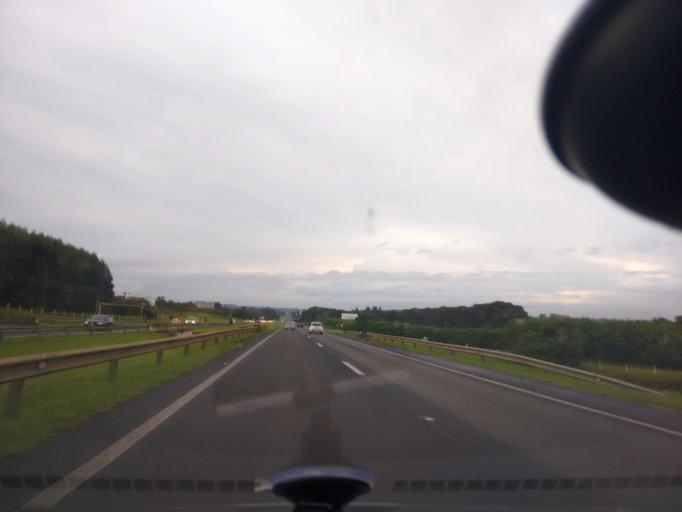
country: BR
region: Sao Paulo
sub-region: Sao Carlos
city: Sao Carlos
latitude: -22.1191
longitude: -47.8142
